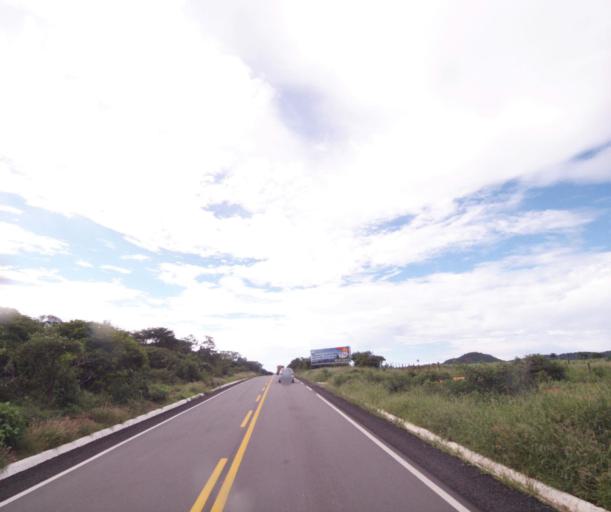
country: BR
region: Bahia
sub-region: Guanambi
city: Guanambi
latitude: -14.3921
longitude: -42.7578
